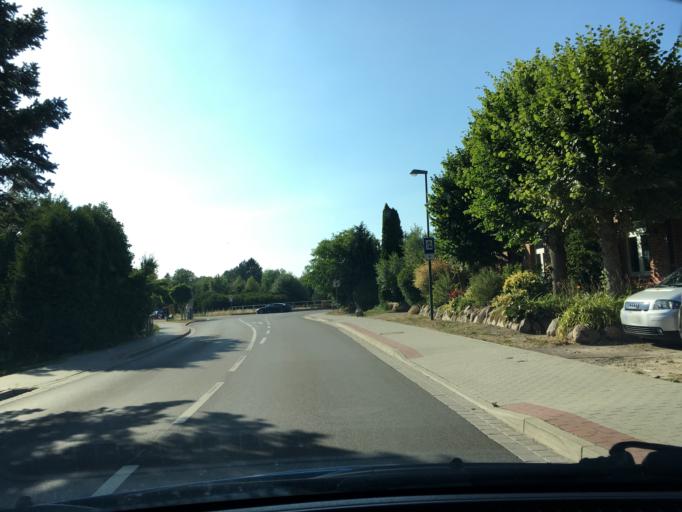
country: DE
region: Lower Saxony
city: Dahlenburg
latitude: 53.1847
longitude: 10.7515
